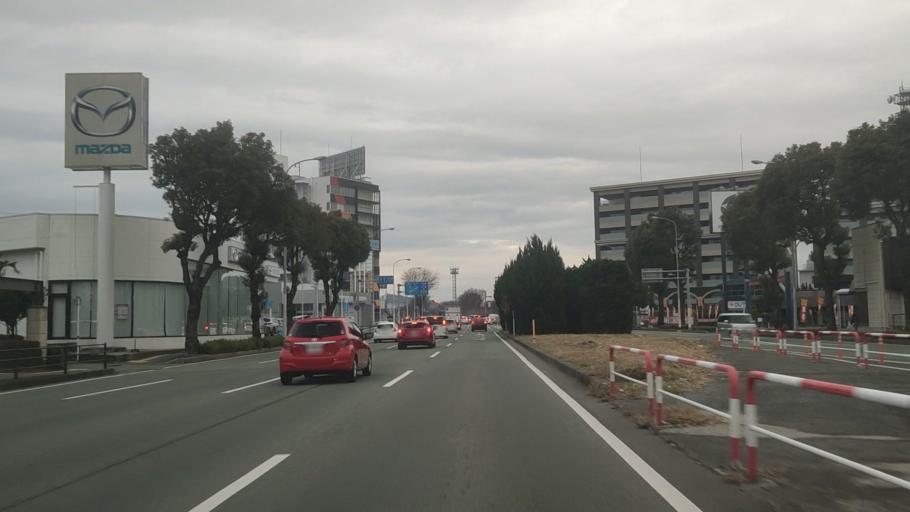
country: JP
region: Kumamoto
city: Kumamoto
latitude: 32.8143
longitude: 130.7502
